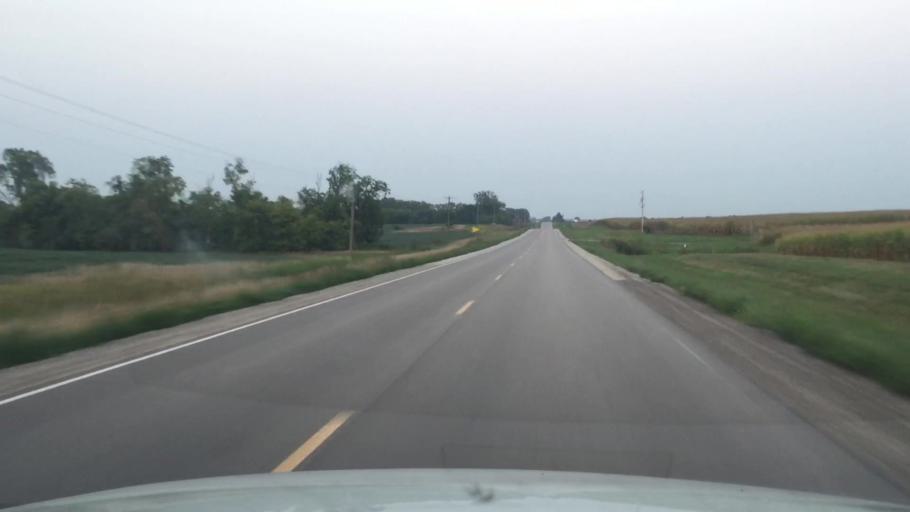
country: US
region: Iowa
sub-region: Warren County
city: Indianola
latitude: 41.1827
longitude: -93.4903
